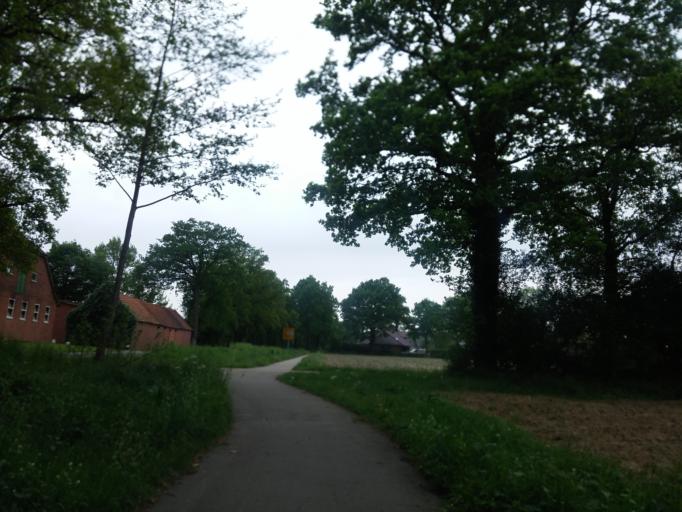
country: DE
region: Lower Saxony
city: Wietmarschen
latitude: 52.5071
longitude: 7.1366
